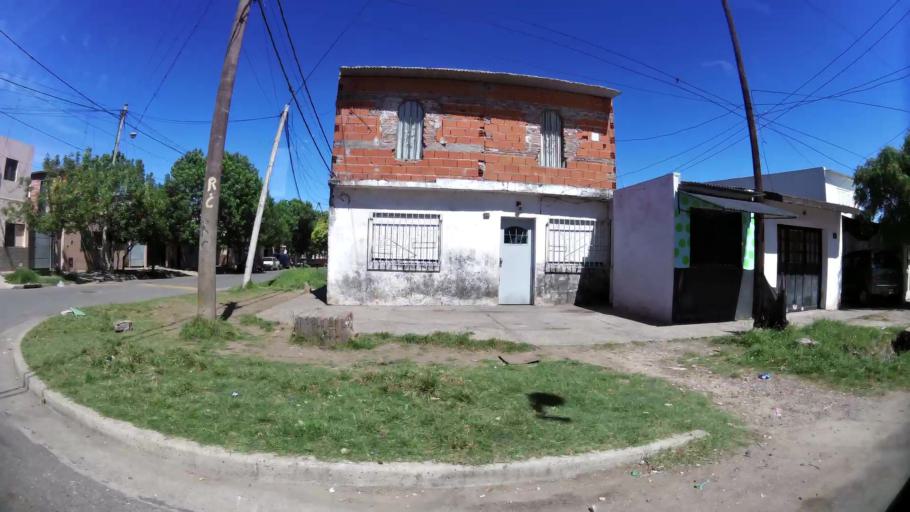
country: AR
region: Santa Fe
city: Perez
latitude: -32.9693
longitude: -60.7068
